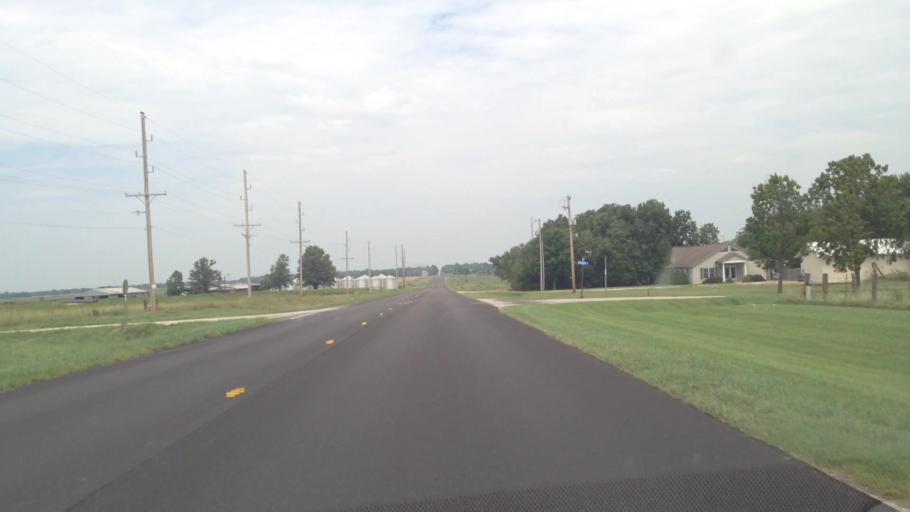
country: US
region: Kansas
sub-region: Allen County
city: Iola
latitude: 37.8922
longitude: -95.1708
